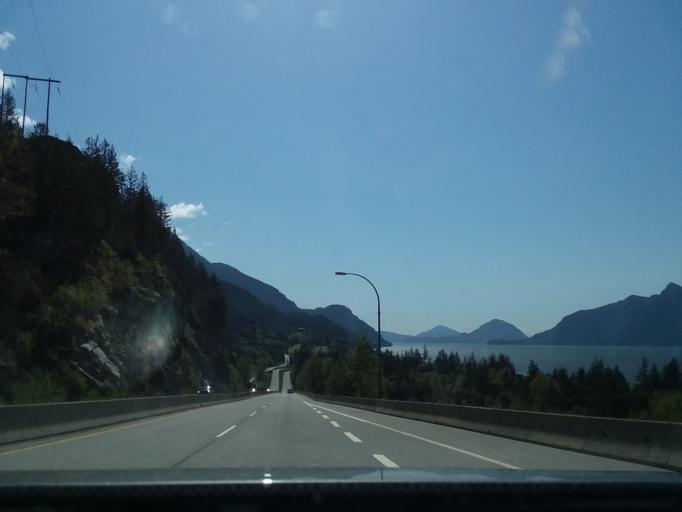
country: CA
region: British Columbia
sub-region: Greater Vancouver Regional District
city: Lions Bay
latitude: 49.5901
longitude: -123.2192
